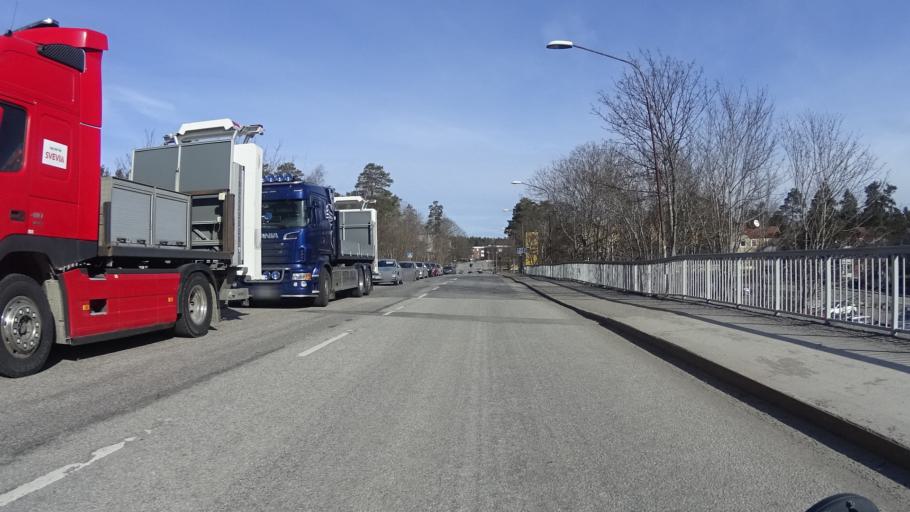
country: SE
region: Stockholm
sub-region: Nacka Kommun
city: Nacka
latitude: 59.2777
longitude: 18.1273
